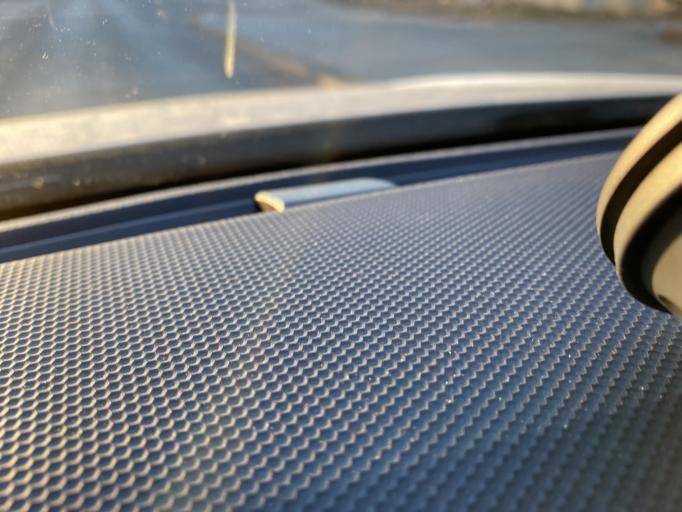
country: FI
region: Pirkanmaa
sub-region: Lounais-Pirkanmaa
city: Punkalaidun
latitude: 61.1169
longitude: 23.0876
